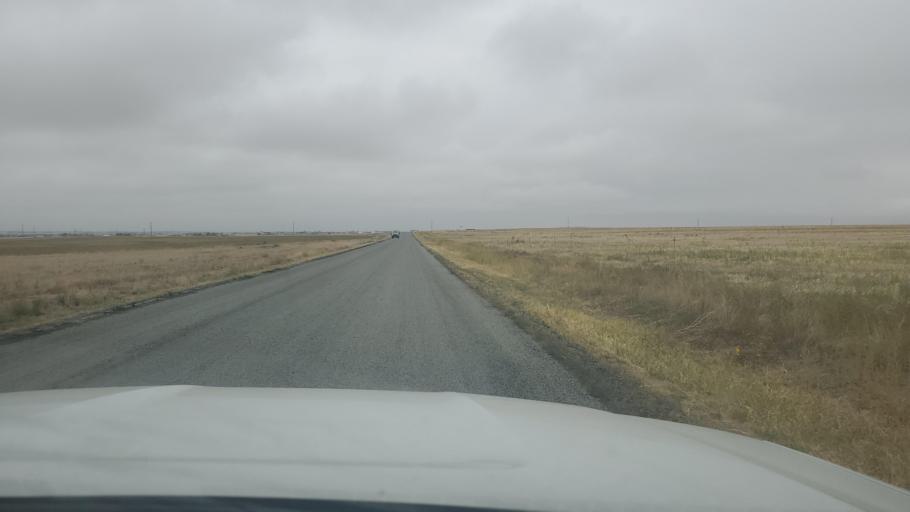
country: US
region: Colorado
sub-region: Weld County
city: Lochbuie
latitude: 39.9292
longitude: -104.6030
